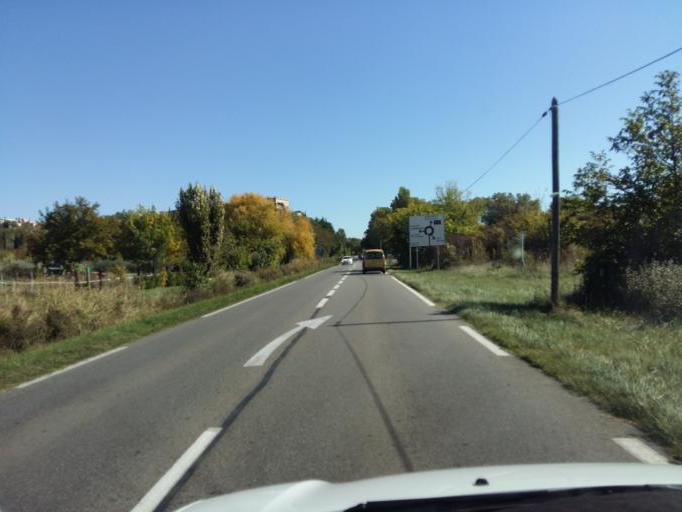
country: FR
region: Provence-Alpes-Cote d'Azur
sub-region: Departement du Vaucluse
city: Lauris
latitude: 43.7468
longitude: 5.3033
